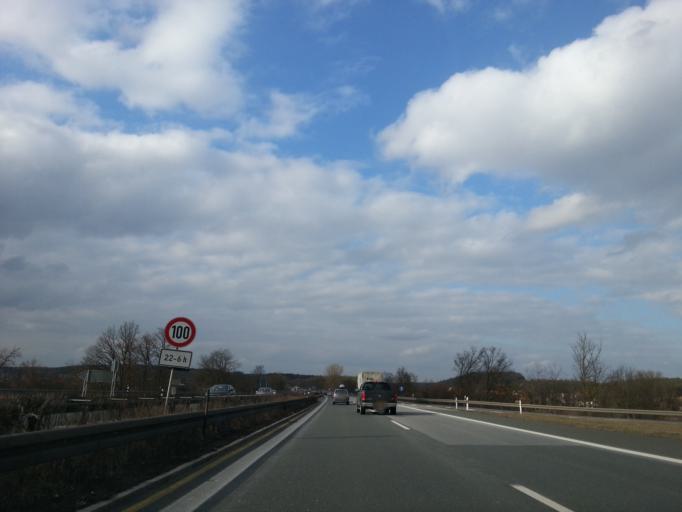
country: DE
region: Bavaria
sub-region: Regierungsbezirk Mittelfranken
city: Gremsdorf
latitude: 49.7004
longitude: 10.8549
